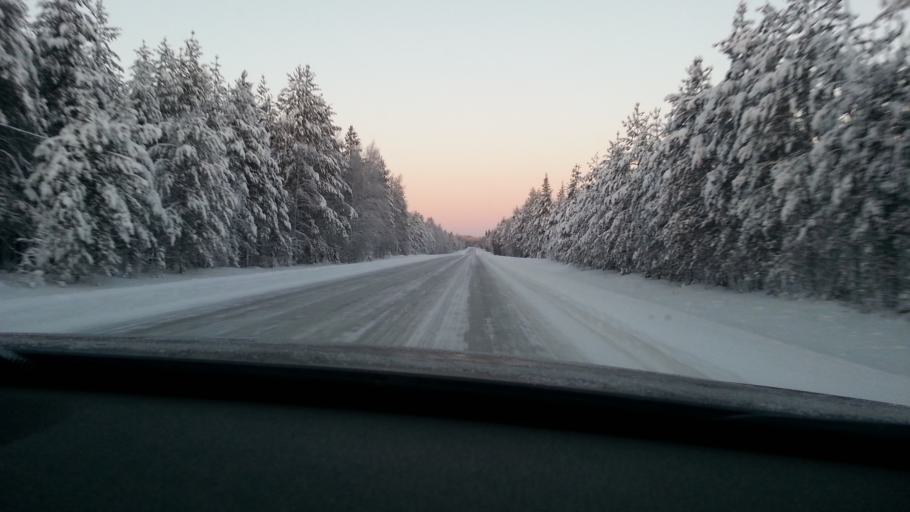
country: FI
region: Lapland
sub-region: Tunturi-Lappi
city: Kittilae
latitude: 67.2224
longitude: 24.9236
